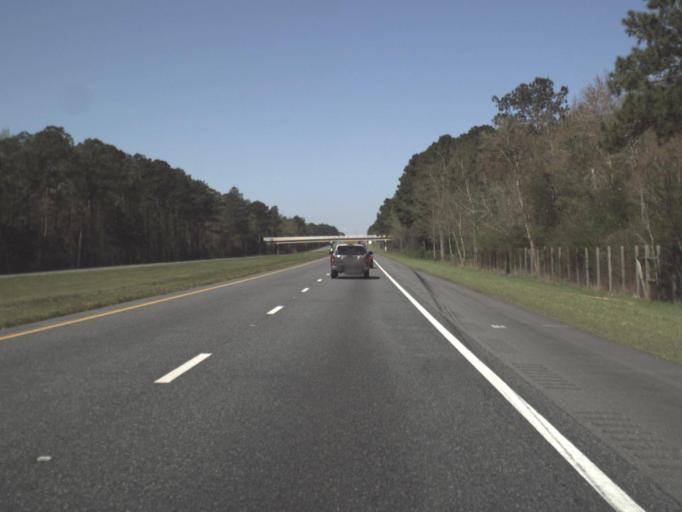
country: US
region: Florida
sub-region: Walton County
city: DeFuniak Springs
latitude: 30.6914
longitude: -86.0902
